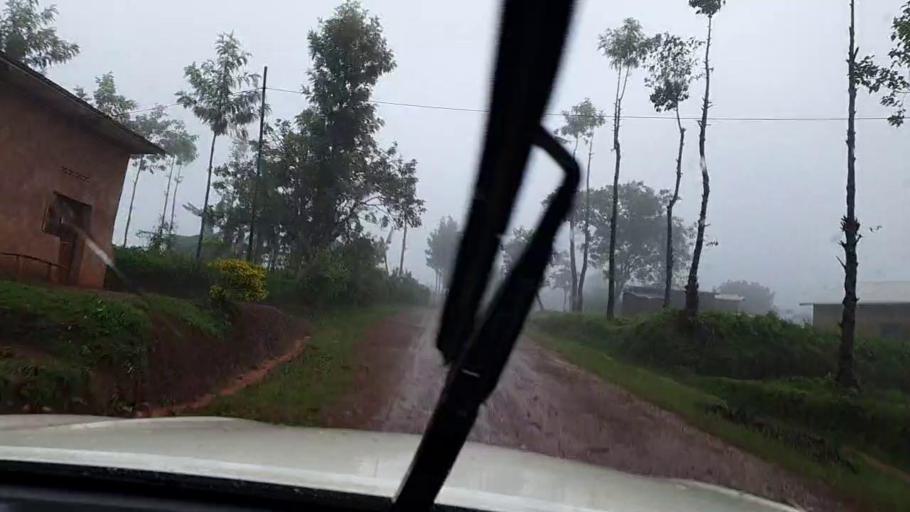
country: RW
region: Northern Province
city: Byumba
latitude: -1.7449
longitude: 30.0041
